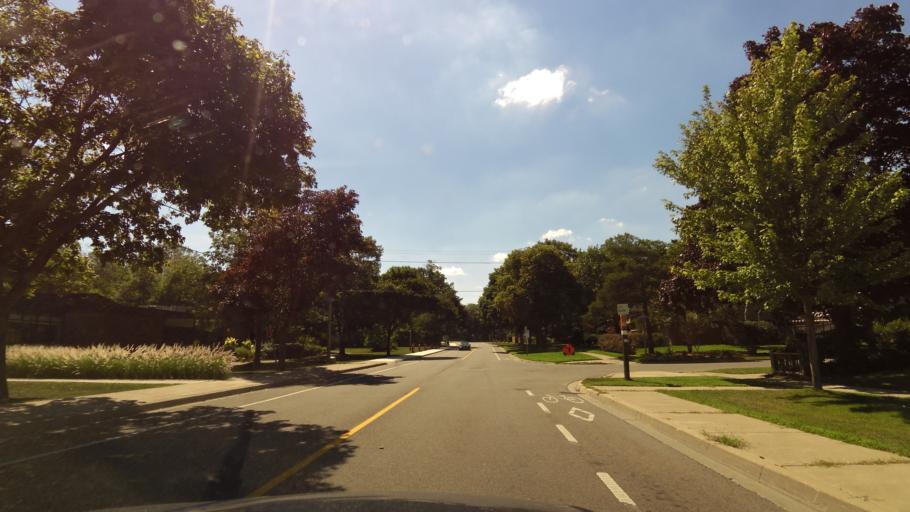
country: CA
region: Ontario
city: Mississauga
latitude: 43.5315
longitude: -79.6273
